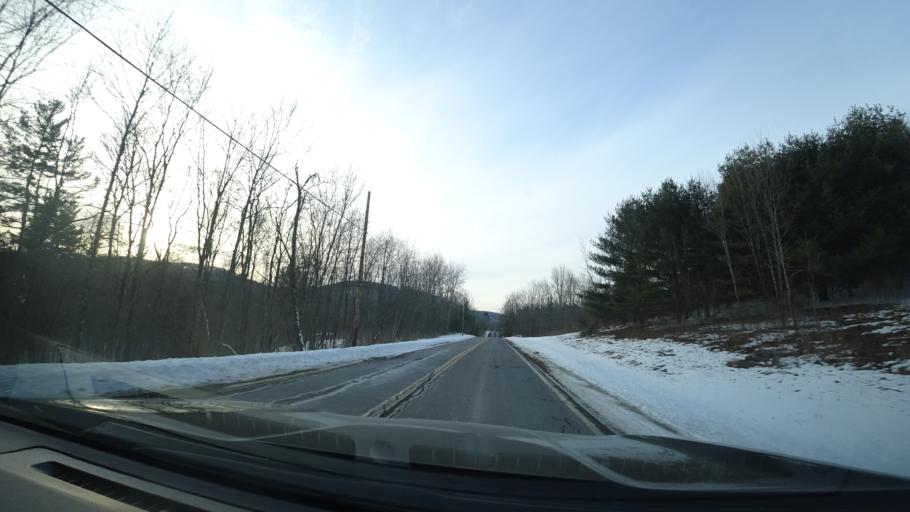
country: US
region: New York
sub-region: Washington County
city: Cambridge
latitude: 43.1741
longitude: -73.3583
